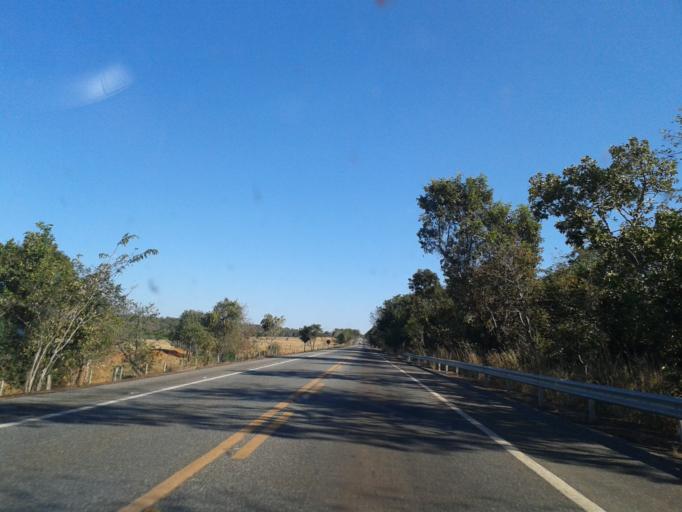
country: BR
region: Goias
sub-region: Mozarlandia
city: Mozarlandia
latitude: -14.8455
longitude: -50.5430
